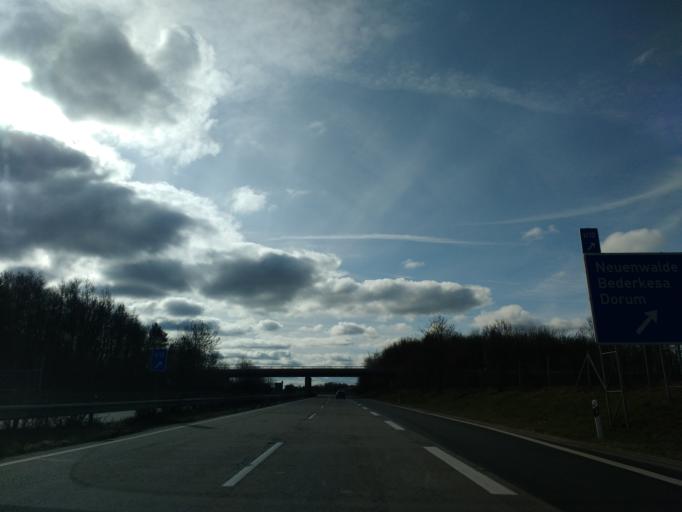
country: DE
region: Lower Saxony
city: Midlum
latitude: 53.6792
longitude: 8.6578
